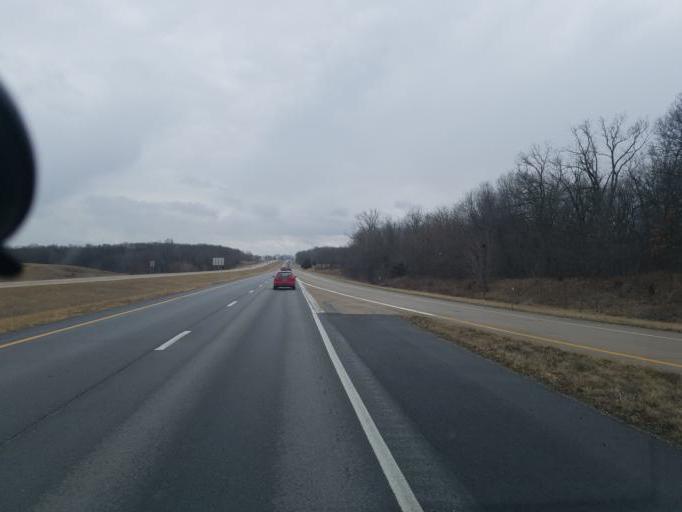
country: US
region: Missouri
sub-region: Randolph County
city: Moberly
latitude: 39.3913
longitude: -92.4133
